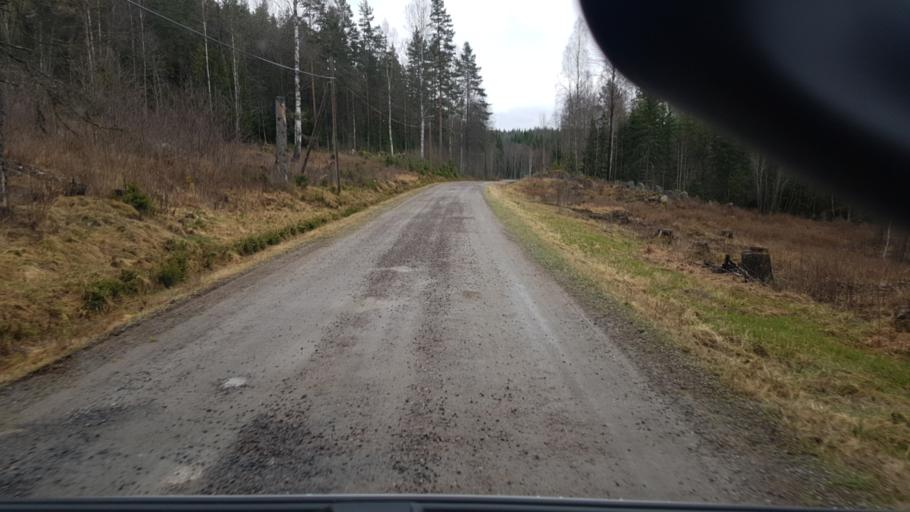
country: SE
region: Vaermland
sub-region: Eda Kommun
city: Charlottenberg
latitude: 59.9315
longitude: 12.3725
